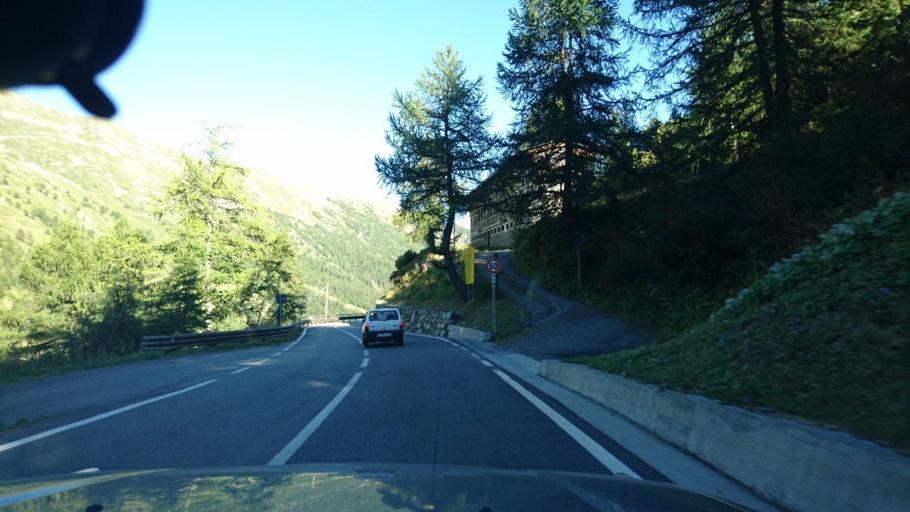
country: IT
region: Aosta Valley
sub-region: Valle d'Aosta
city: San Leonardo
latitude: 45.8501
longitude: 7.1595
